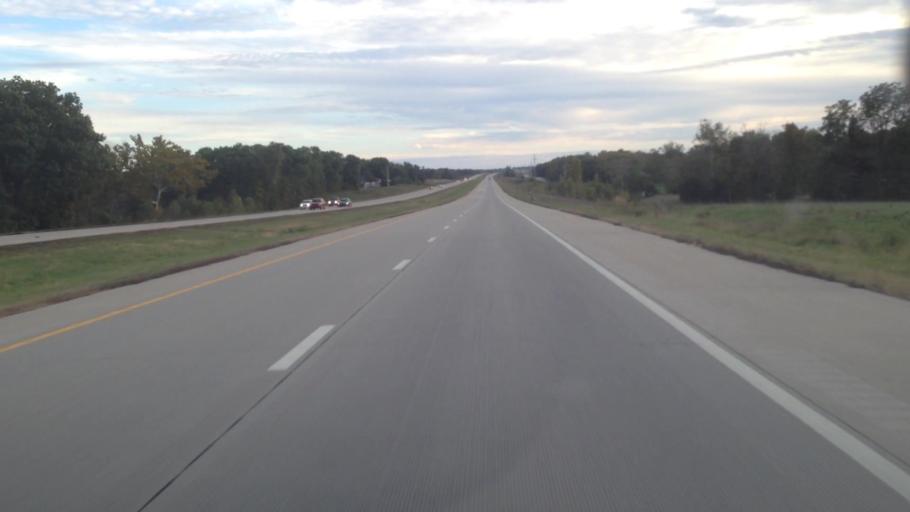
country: US
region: Kansas
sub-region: Douglas County
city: Baldwin City
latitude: 38.7579
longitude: -95.2683
